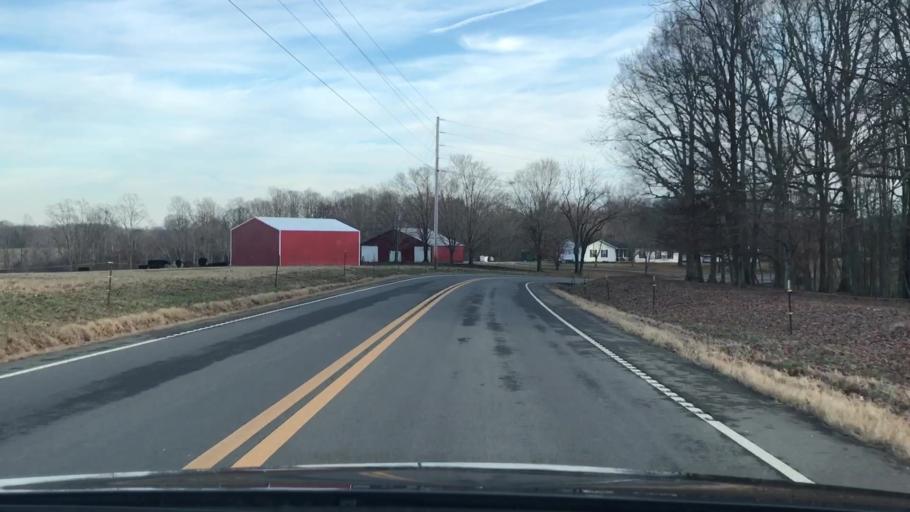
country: US
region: Tennessee
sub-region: Macon County
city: Red Boiling Springs
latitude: 36.5579
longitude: -85.8369
